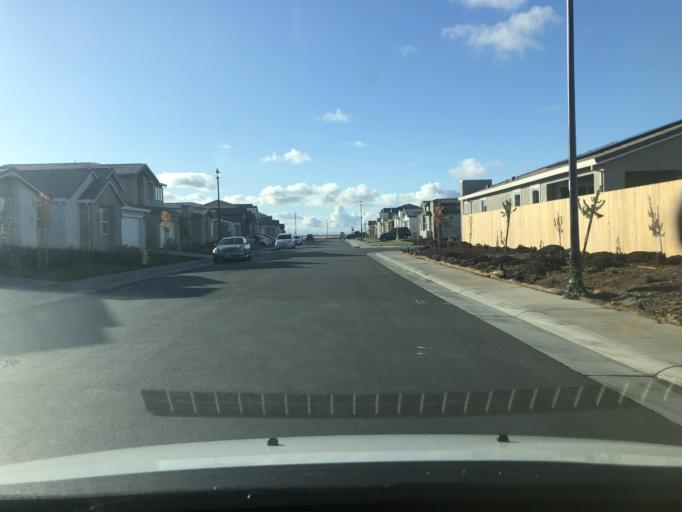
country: US
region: California
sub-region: Sacramento County
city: Antelope
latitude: 38.7695
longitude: -121.3877
